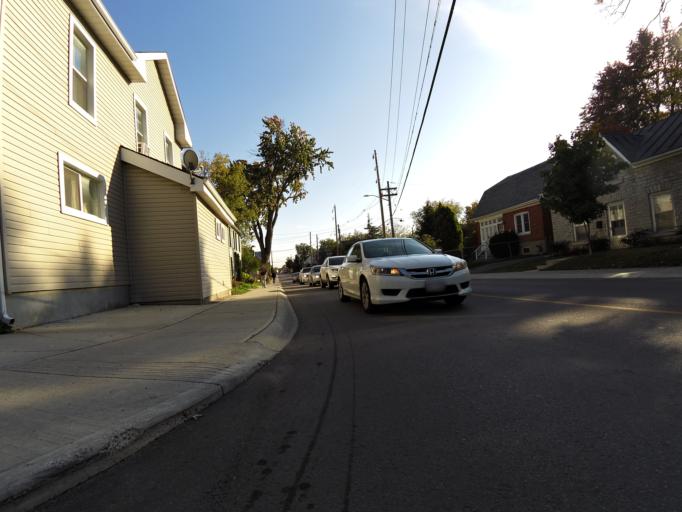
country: CA
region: Ontario
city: Kingston
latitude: 44.2376
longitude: -76.4941
